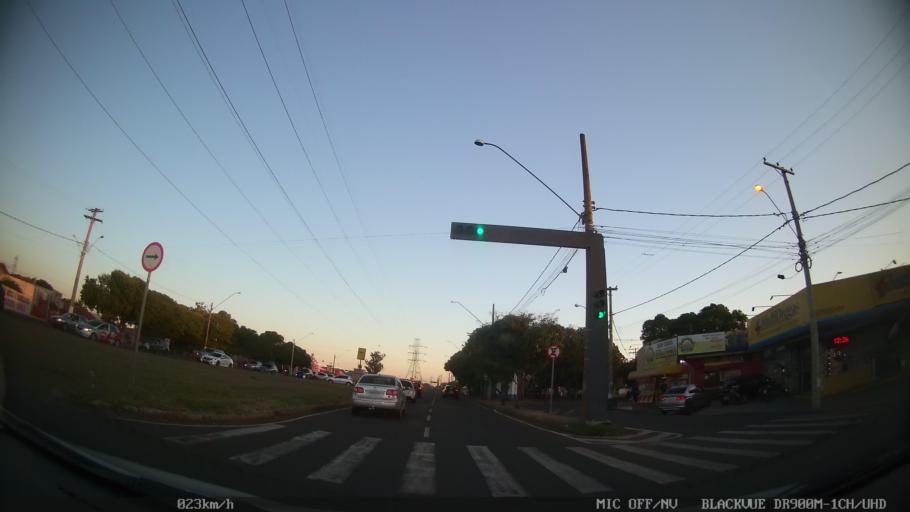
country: BR
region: Sao Paulo
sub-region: Sao Jose Do Rio Preto
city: Sao Jose do Rio Preto
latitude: -20.7936
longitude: -49.3448
